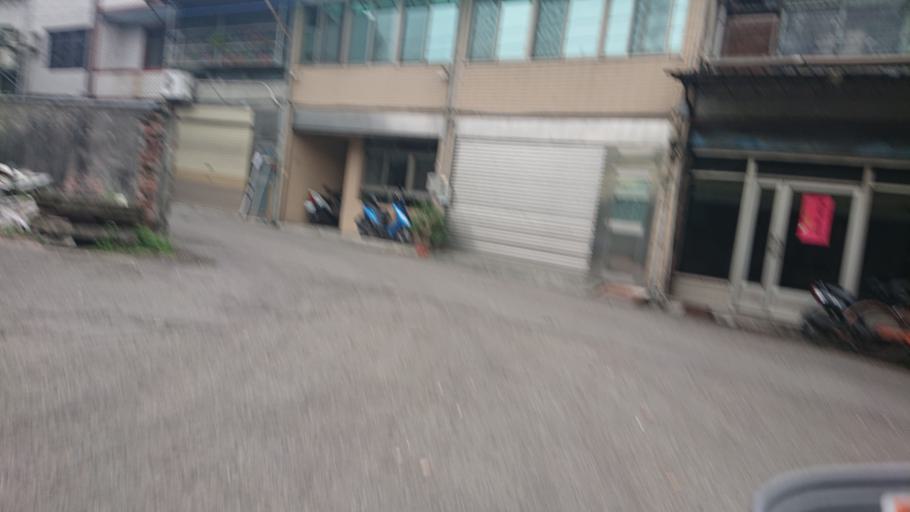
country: TW
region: Taiwan
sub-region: Taoyuan
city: Taoyuan
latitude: 24.9418
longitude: 121.3578
